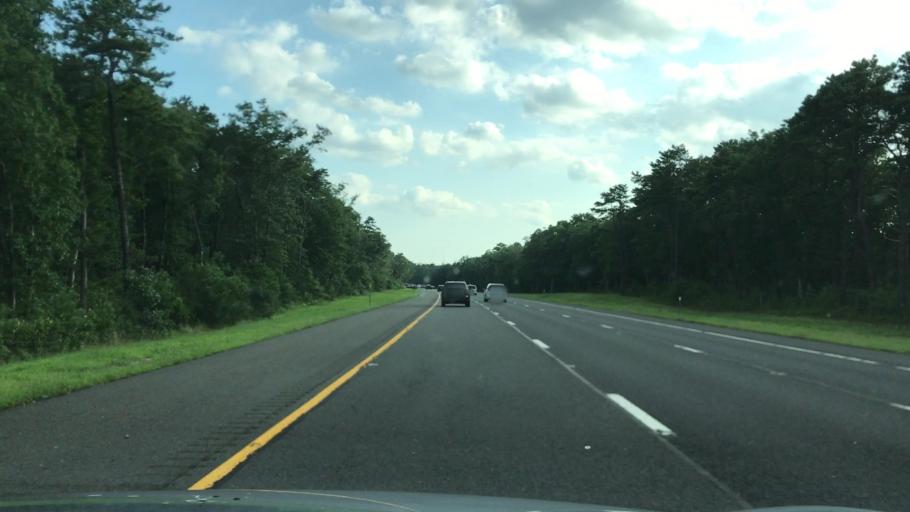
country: US
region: New Jersey
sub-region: Ocean County
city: Manahawkin
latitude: 39.6961
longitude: -74.2955
